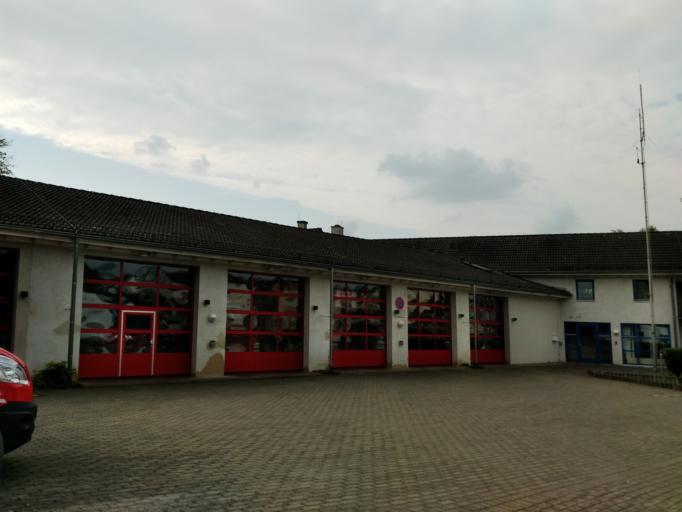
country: DE
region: North Rhine-Westphalia
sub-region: Regierungsbezirk Koln
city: Bad Honnef
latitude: 50.6406
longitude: 7.2278
